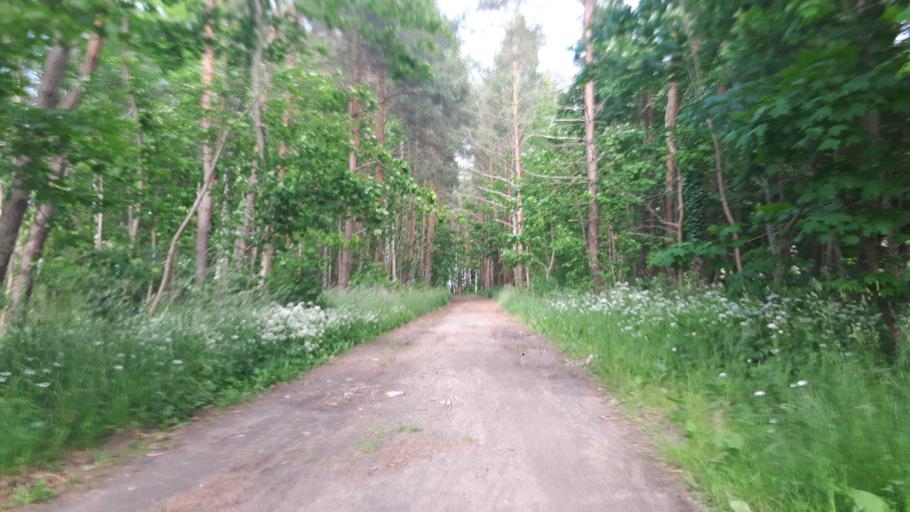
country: PL
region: Pomeranian Voivodeship
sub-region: Slupsk
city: Slupsk
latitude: 54.6003
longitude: 17.0128
